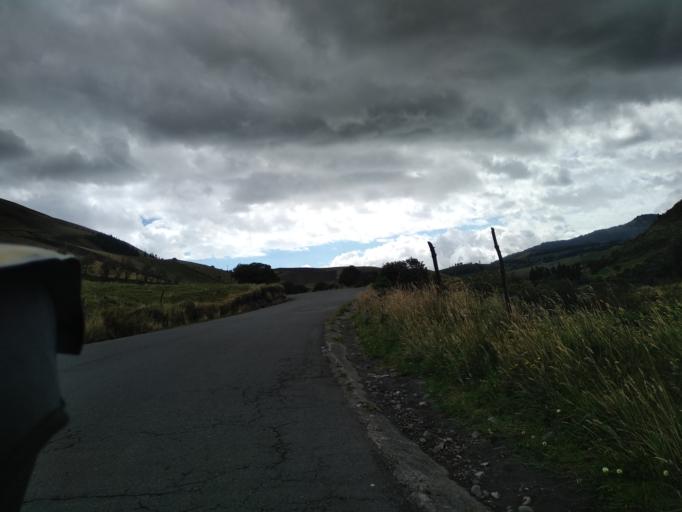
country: EC
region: Cotopaxi
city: Saquisili
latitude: -0.7262
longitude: -78.7590
